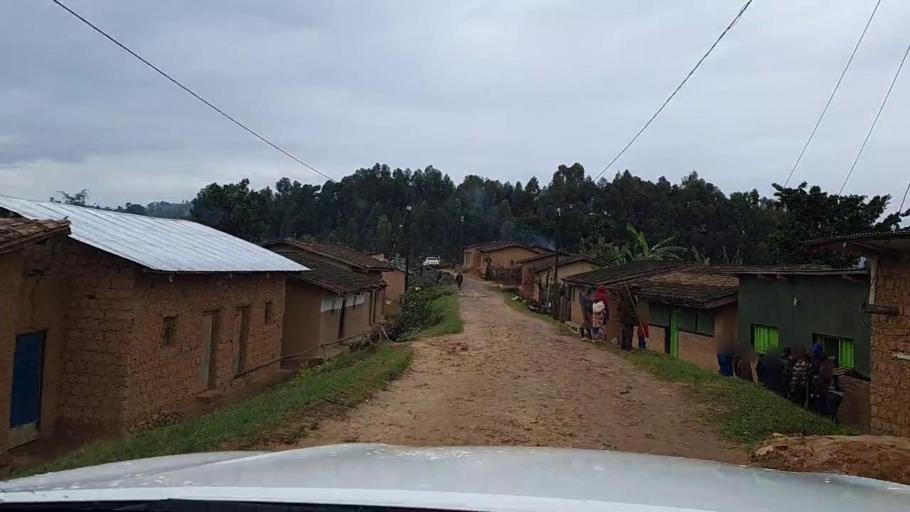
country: RW
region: Southern Province
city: Nzega
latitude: -2.4556
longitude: 29.4687
